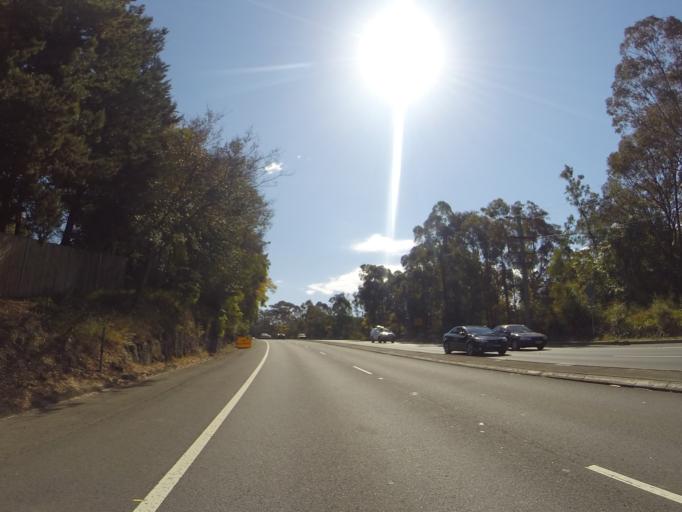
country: AU
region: New South Wales
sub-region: Blue Mountains Municipality
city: Blaxland
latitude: -33.7007
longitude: 150.5742
